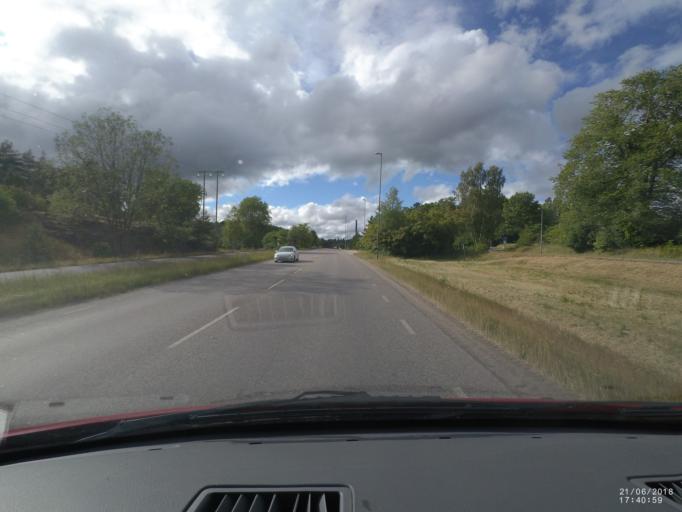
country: SE
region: Soedermanland
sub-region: Nykopings Kommun
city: Nykoping
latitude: 58.7645
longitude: 17.0292
